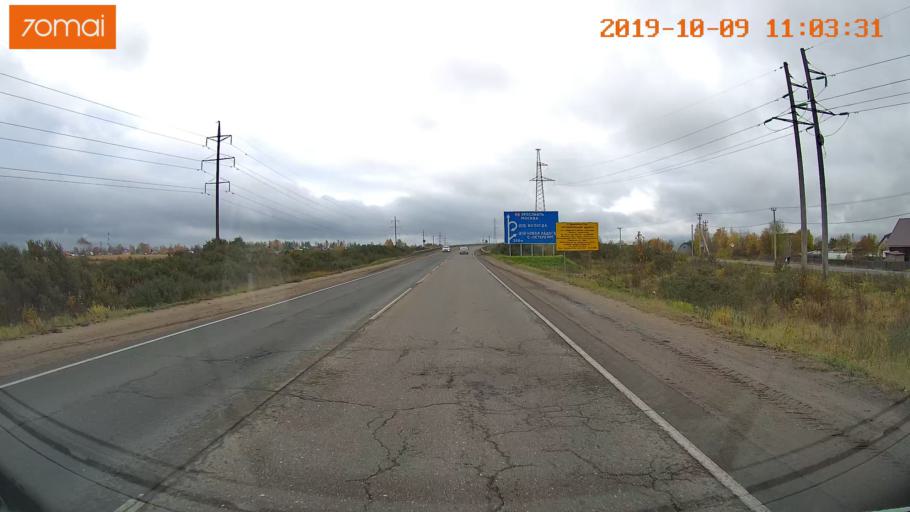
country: RU
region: Vologda
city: Vologda
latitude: 59.2211
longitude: 39.7742
